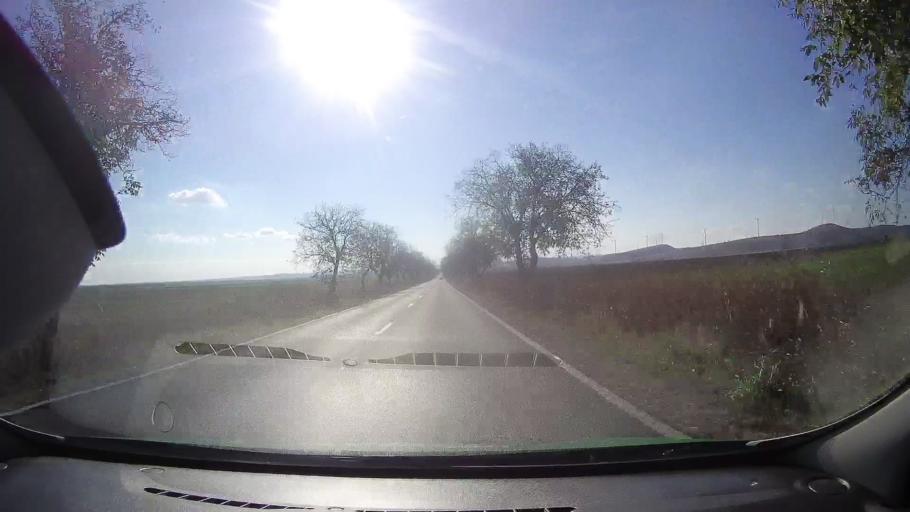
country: RO
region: Tulcea
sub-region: Comuna Ceamurlia de Jos
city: Ceamurlia de Jos
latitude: 44.8011
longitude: 28.6906
